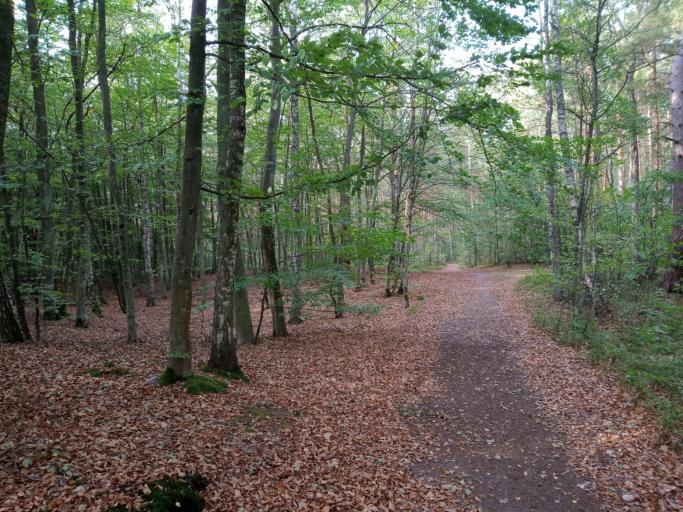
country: PL
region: Pomeranian Voivodeship
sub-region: Powiat nowodworski
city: Stegna
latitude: 54.3382
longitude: 19.0984
